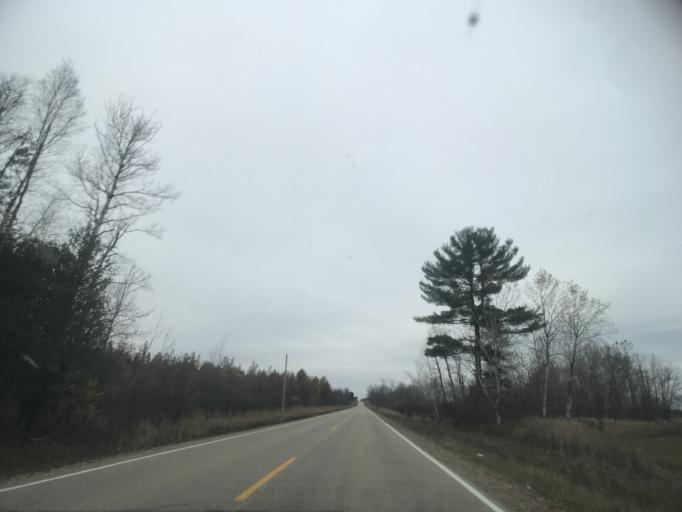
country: US
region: Wisconsin
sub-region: Oconto County
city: Gillett
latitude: 44.9834
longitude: -88.3025
